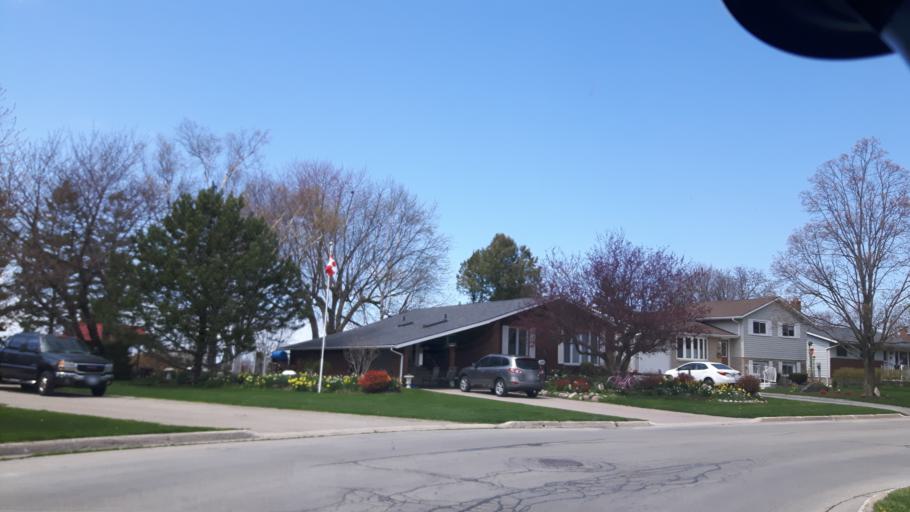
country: CA
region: Ontario
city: Goderich
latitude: 43.7305
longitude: -81.7199
